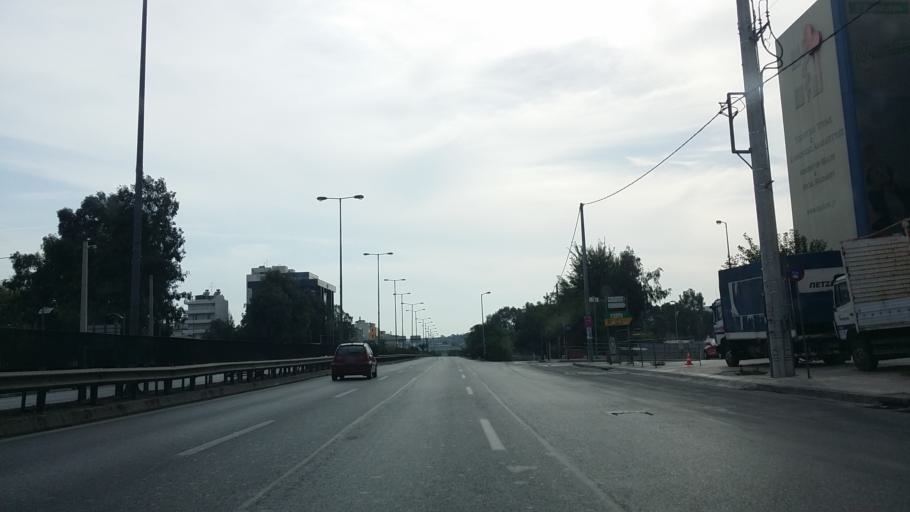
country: GR
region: Attica
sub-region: Nomarchia Athinas
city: Khalandrion
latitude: 38.0340
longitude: 23.7957
